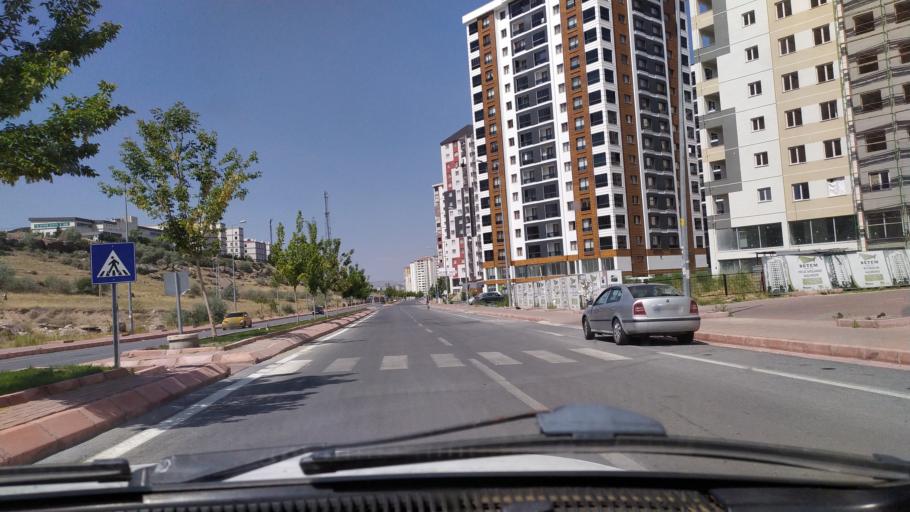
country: TR
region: Kayseri
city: Talas
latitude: 38.7097
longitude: 35.5569
